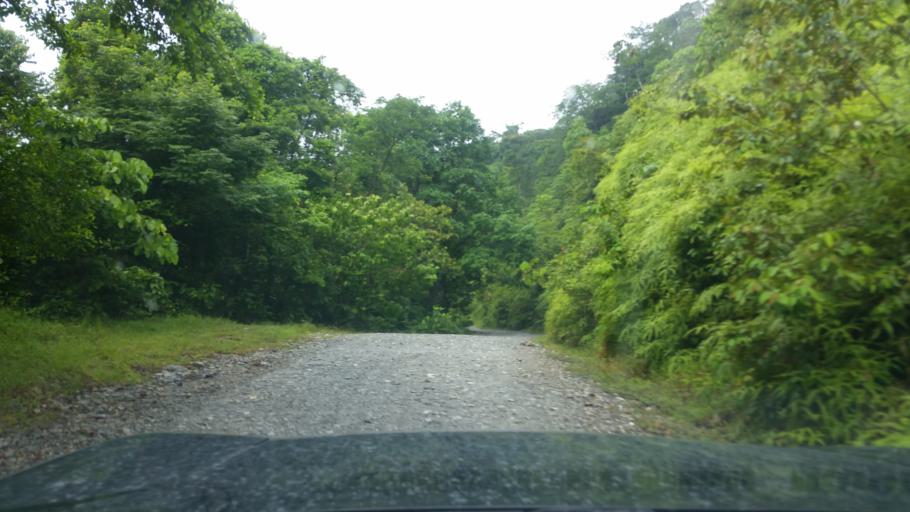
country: NI
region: Atlantico Norte (RAAN)
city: Bonanza
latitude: 14.0633
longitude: -84.6203
